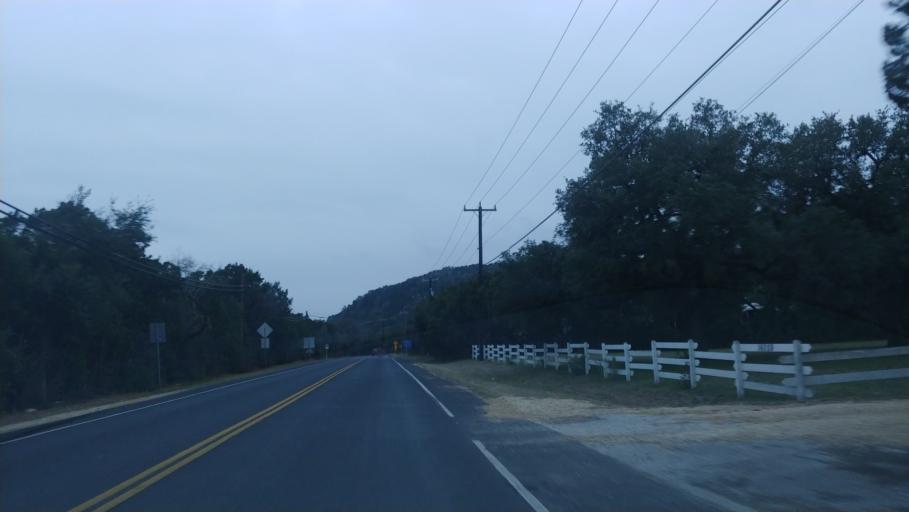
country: US
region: Texas
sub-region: Bexar County
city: Helotes
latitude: 29.5923
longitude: -98.6891
